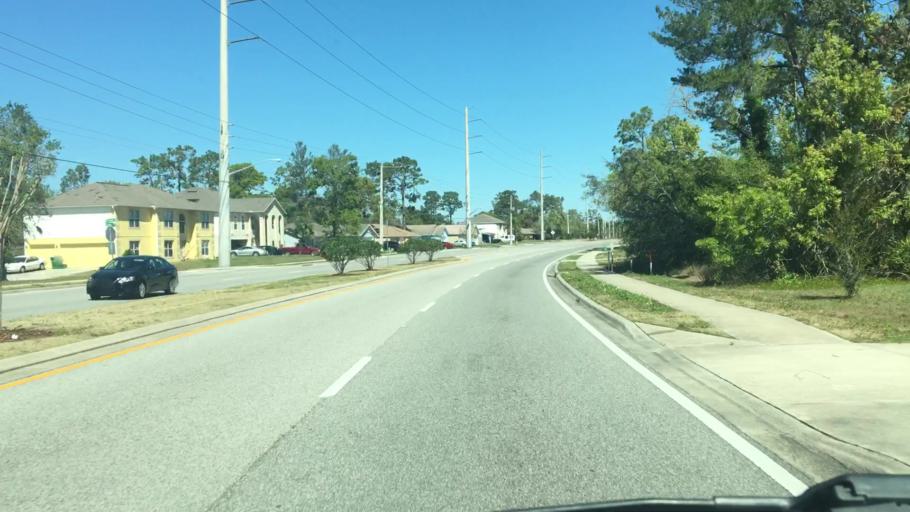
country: US
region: Florida
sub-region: Volusia County
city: Deltona
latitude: 28.9106
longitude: -81.1810
